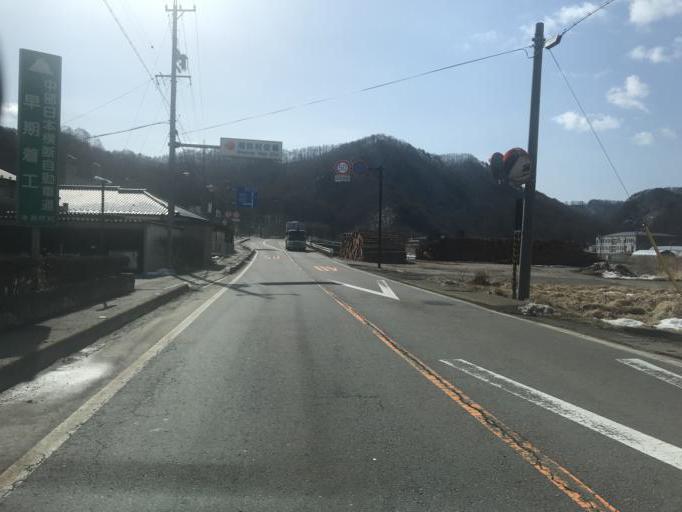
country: JP
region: Nagano
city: Saku
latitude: 36.0208
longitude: 138.4917
